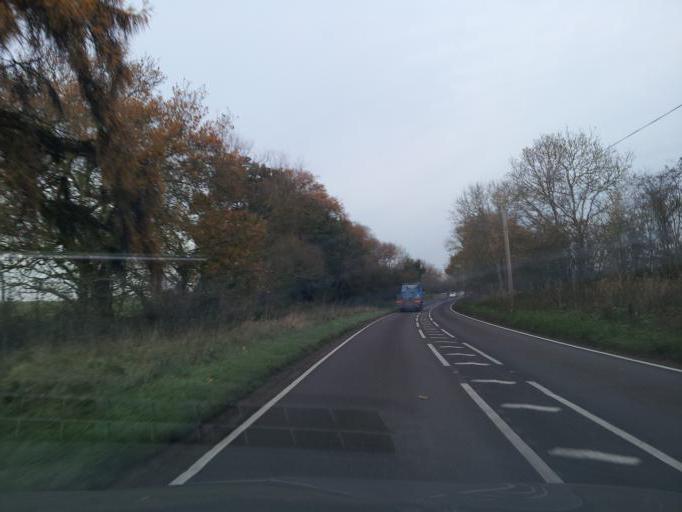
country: GB
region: England
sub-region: Buckinghamshire
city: Stewkley
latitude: 51.8727
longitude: -0.7535
